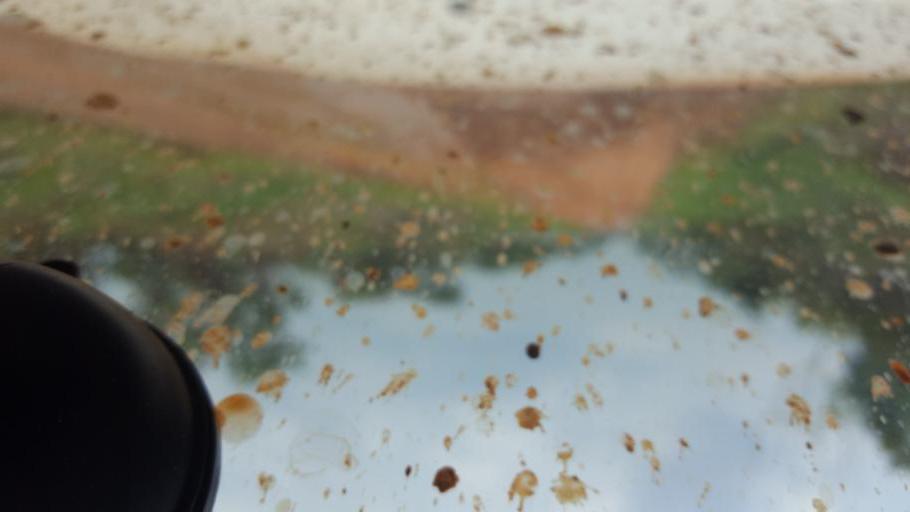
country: CD
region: Bandundu
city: Bandundu
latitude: -3.7608
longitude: 17.1519
